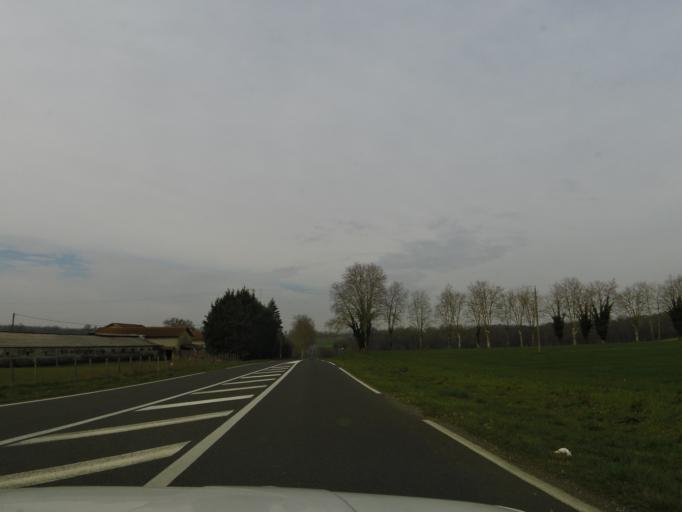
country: FR
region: Rhone-Alpes
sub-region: Departement de l'Ain
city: Perouges
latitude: 45.9498
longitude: 5.1748
